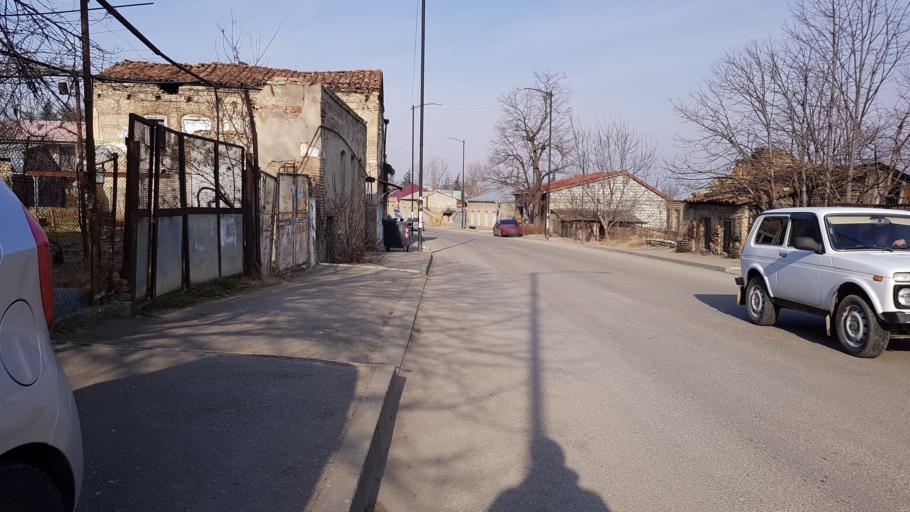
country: GE
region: Kakheti
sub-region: Telavi
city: Telavi
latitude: 41.9247
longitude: 45.4583
